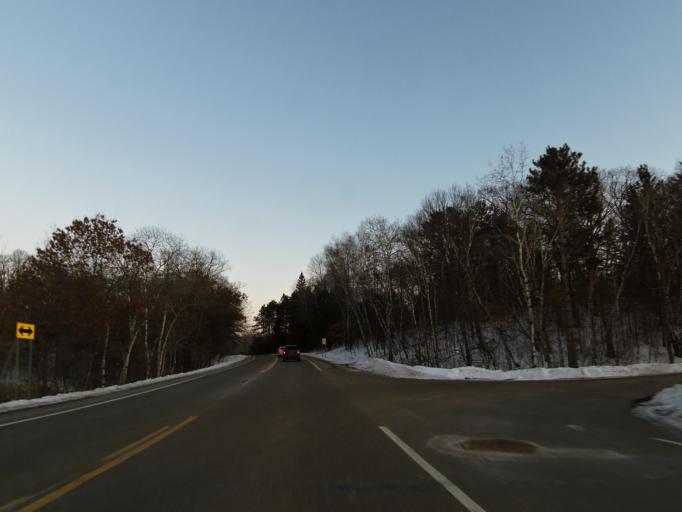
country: US
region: Minnesota
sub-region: Washington County
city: Grant
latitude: 45.0796
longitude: -92.8962
